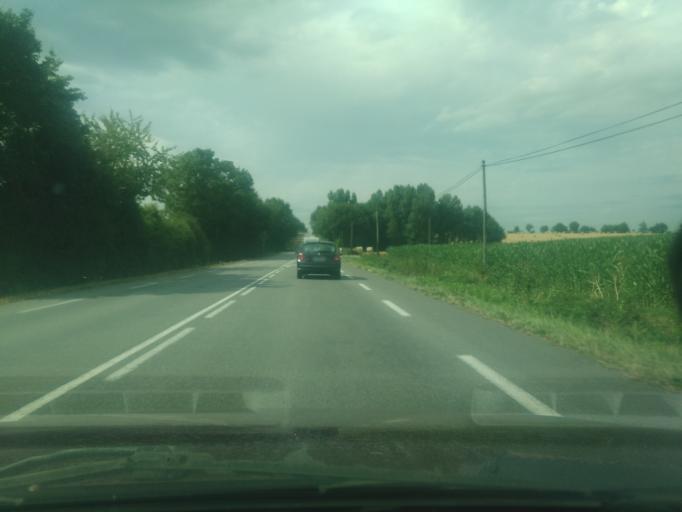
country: FR
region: Pays de la Loire
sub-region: Departement de la Vendee
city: Vendrennes
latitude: 46.7843
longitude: -1.1195
